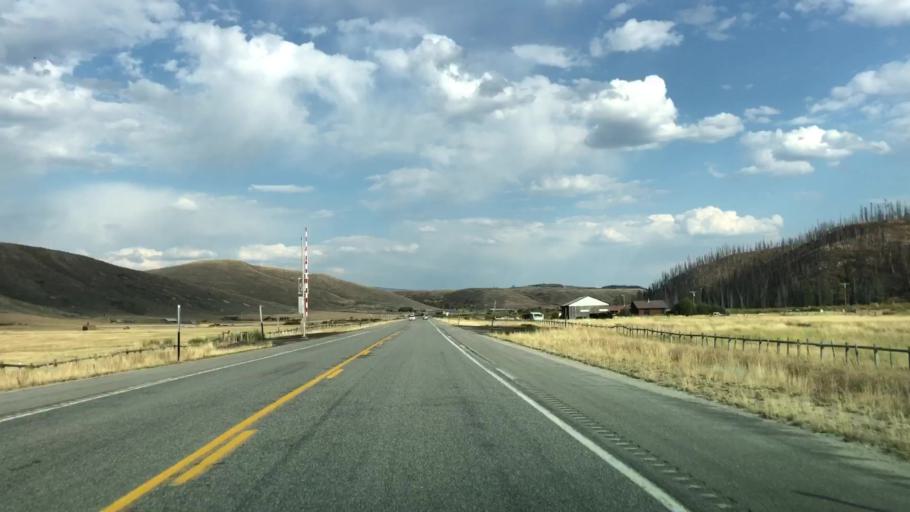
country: US
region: Wyoming
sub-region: Teton County
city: Hoback
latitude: 43.2476
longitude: -110.4712
